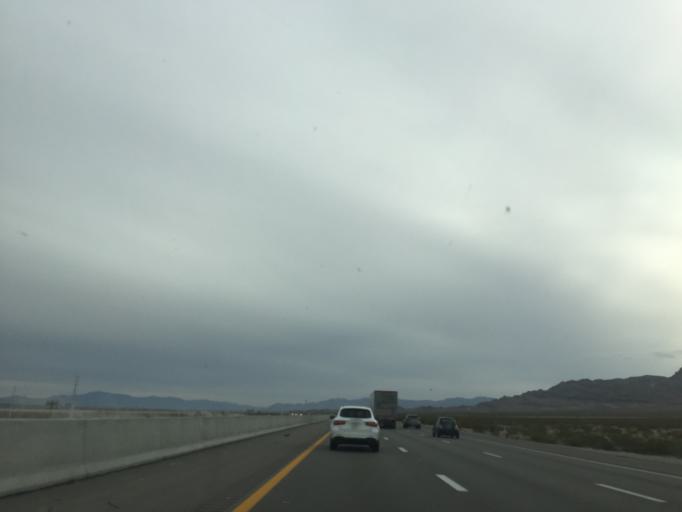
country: US
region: Nevada
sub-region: Clark County
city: Sandy Valley
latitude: 35.6932
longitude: -115.3730
